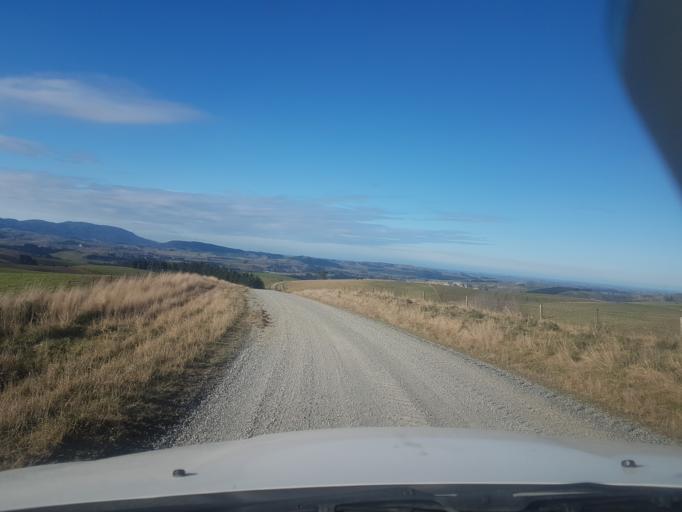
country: NZ
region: Canterbury
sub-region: Timaru District
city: Pleasant Point
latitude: -44.1676
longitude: 170.9063
